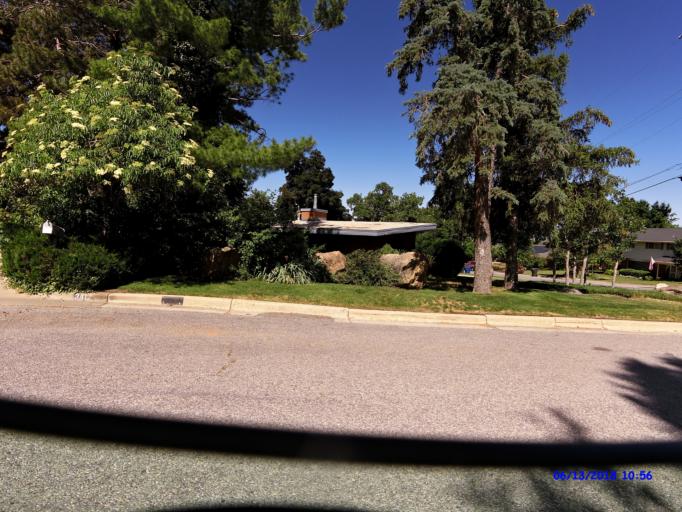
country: US
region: Utah
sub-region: Weber County
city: South Ogden
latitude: 41.2012
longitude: -111.9377
